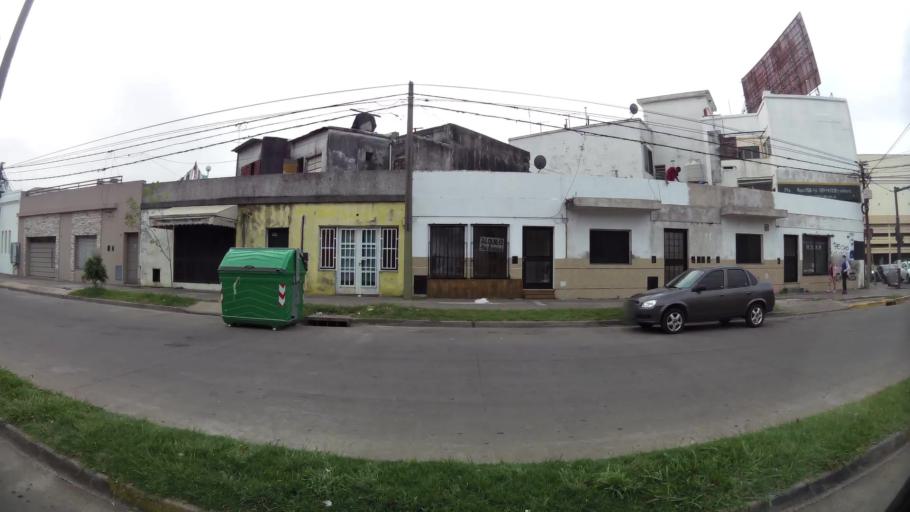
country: AR
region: Santa Fe
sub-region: Departamento de Rosario
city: Rosario
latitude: -32.9129
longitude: -60.6844
